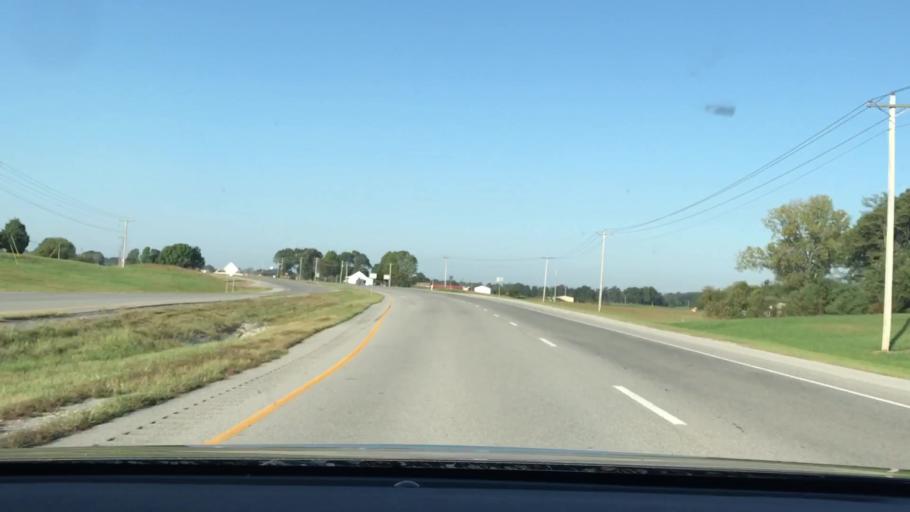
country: US
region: Kentucky
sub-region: Trigg County
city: Cadiz
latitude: 36.8766
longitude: -87.7493
